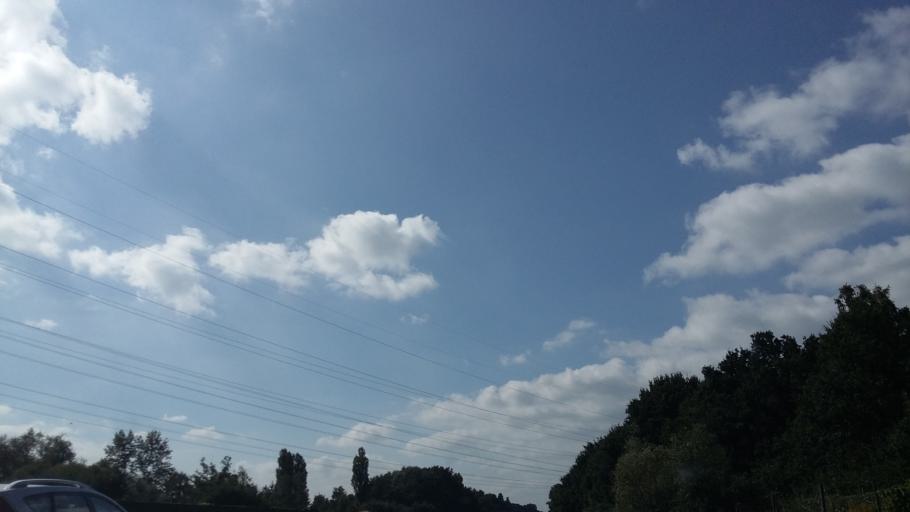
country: DE
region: Bremen
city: Bremen
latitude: 53.1171
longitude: 8.8089
